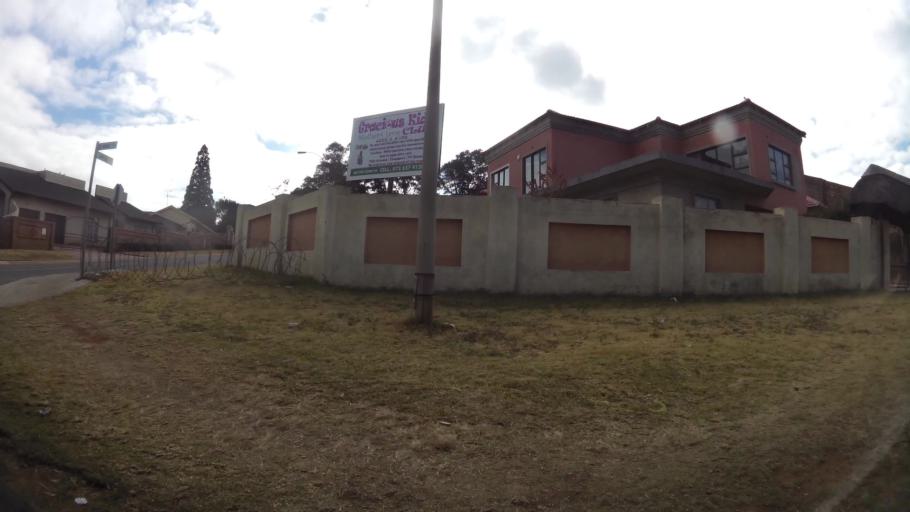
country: ZA
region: Gauteng
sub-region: City of Johannesburg Metropolitan Municipality
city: Roodepoort
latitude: -26.1998
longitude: 27.9122
